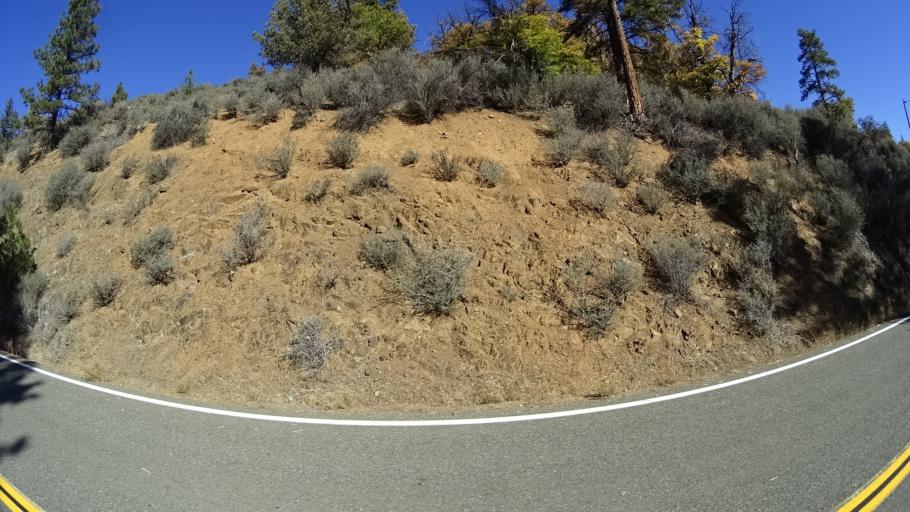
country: US
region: California
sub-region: Siskiyou County
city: Weed
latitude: 41.2958
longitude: -122.8252
